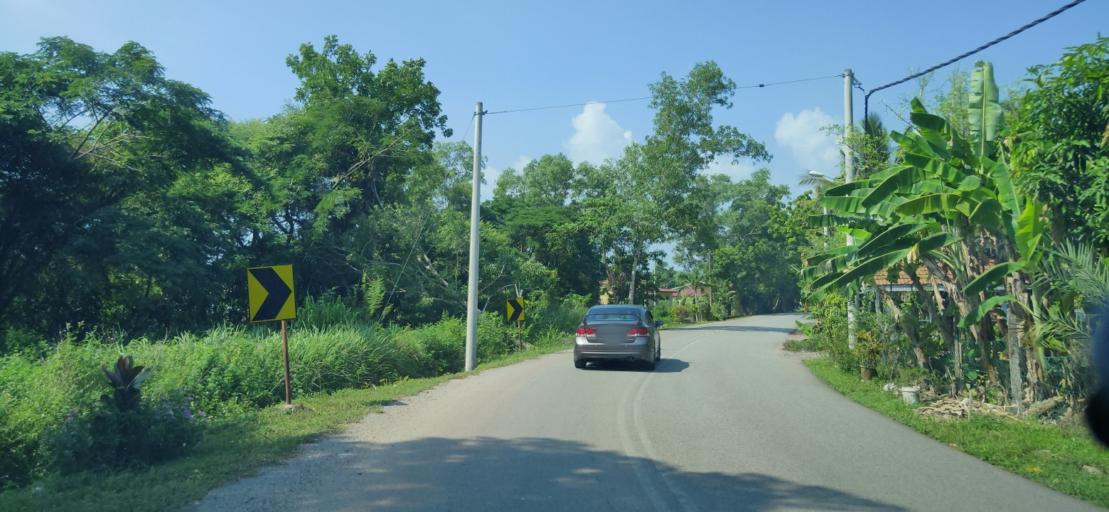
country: MY
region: Kedah
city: Sungai Petani
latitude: 5.6541
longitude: 100.4632
